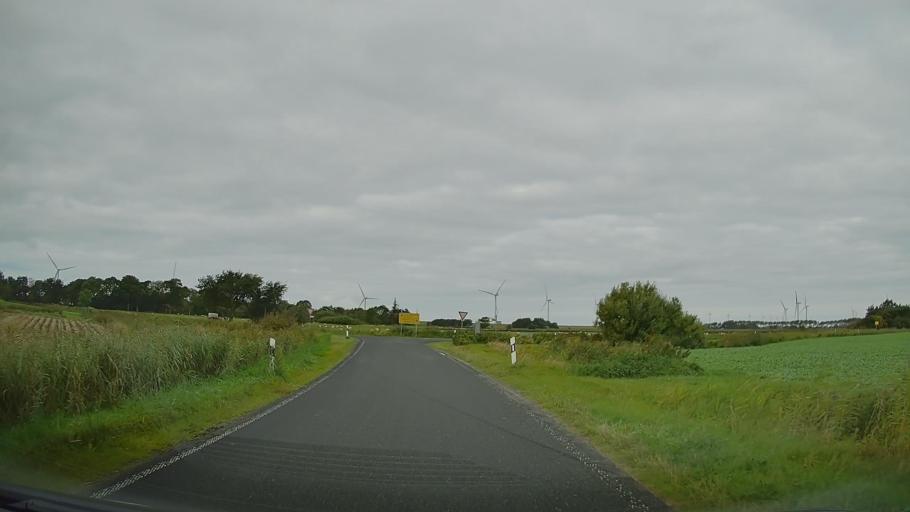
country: DE
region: Schleswig-Holstein
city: Friedrich-Wilhelm-Lubke-Koog
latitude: 54.8277
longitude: 8.6538
